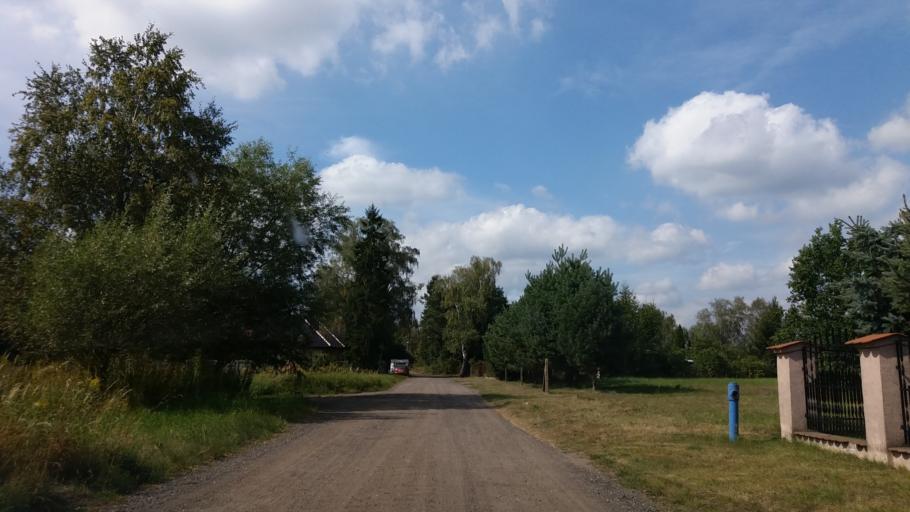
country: PL
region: West Pomeranian Voivodeship
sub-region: Powiat stargardzki
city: Kobylanka
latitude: 53.3560
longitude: 14.9223
